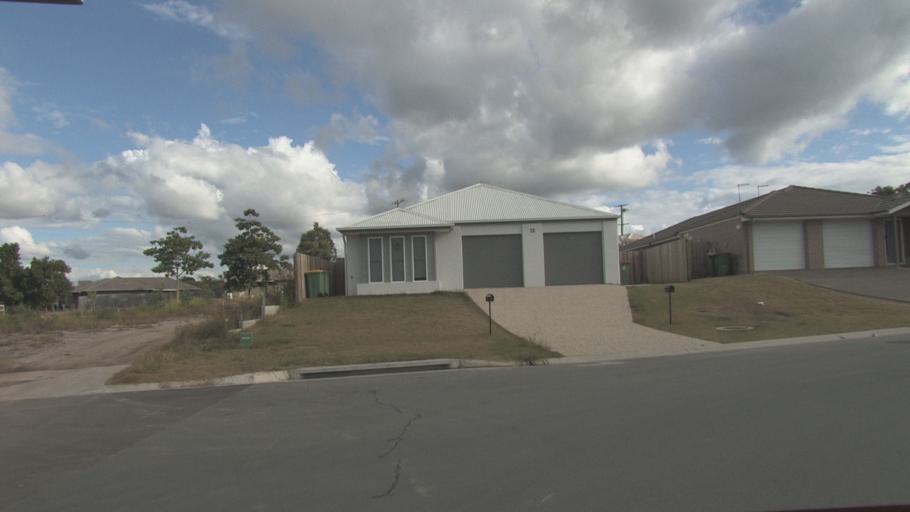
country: AU
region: Queensland
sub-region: Logan
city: Logan Reserve
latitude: -27.6942
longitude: 153.0964
